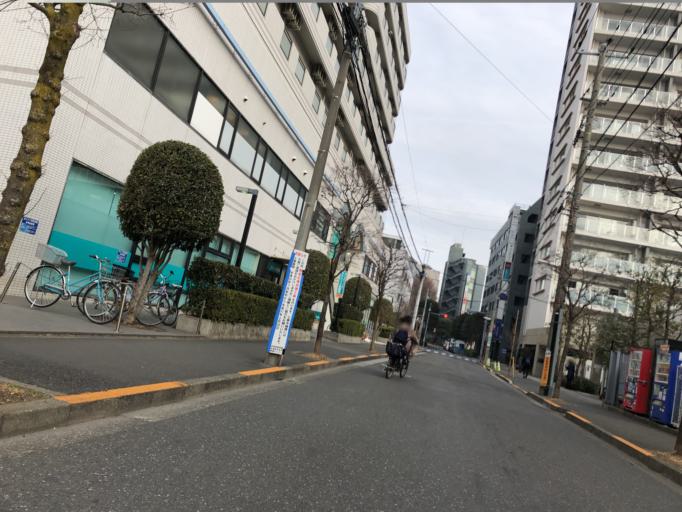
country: JP
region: Tokyo
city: Kamirenjaku
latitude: 35.6998
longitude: 139.5440
